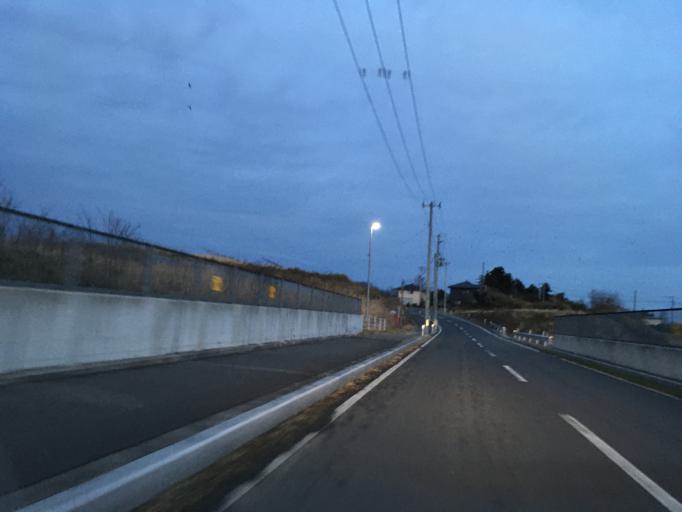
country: JP
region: Miyagi
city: Kogota
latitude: 38.6946
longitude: 141.0976
